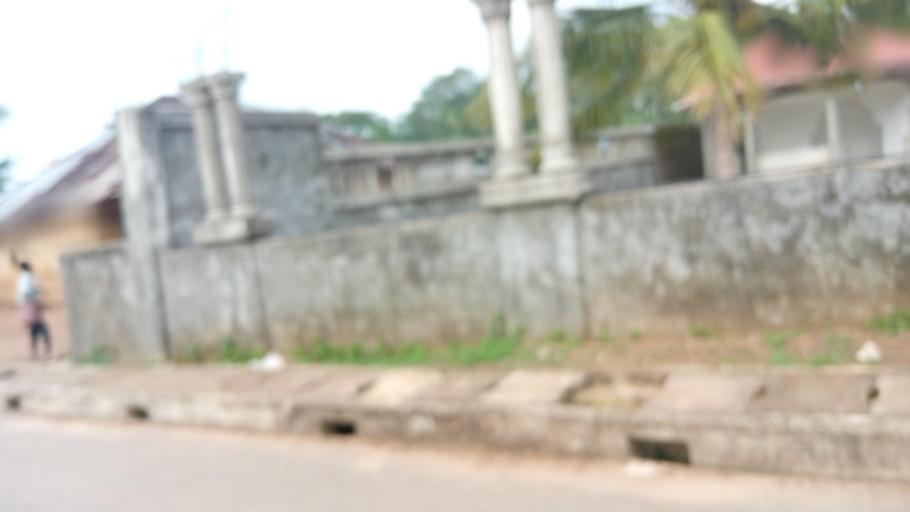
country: SL
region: Southern Province
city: Pujehun
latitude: 7.3491
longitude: -11.7185
